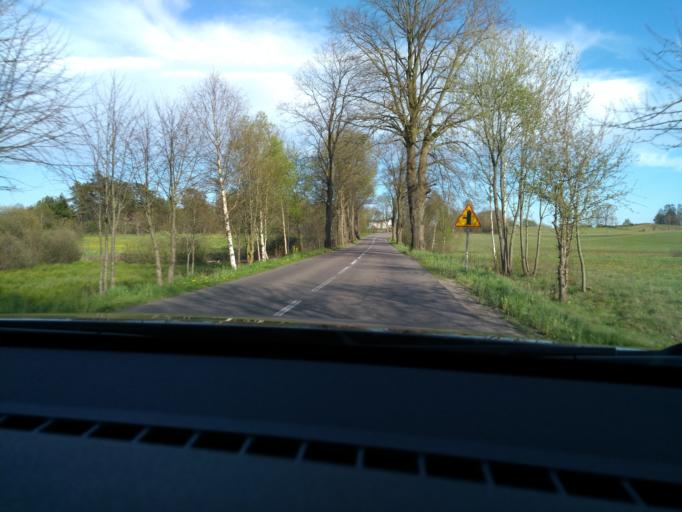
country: PL
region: Pomeranian Voivodeship
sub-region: Powiat leborski
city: Cewice
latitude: 54.3388
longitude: 17.7598
